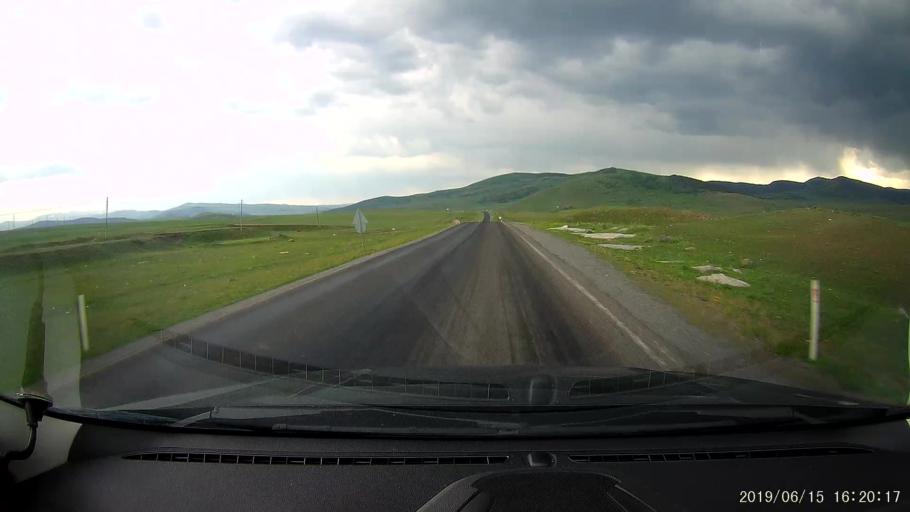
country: TR
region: Ardahan
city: Hanak
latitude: 41.2169
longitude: 42.8483
